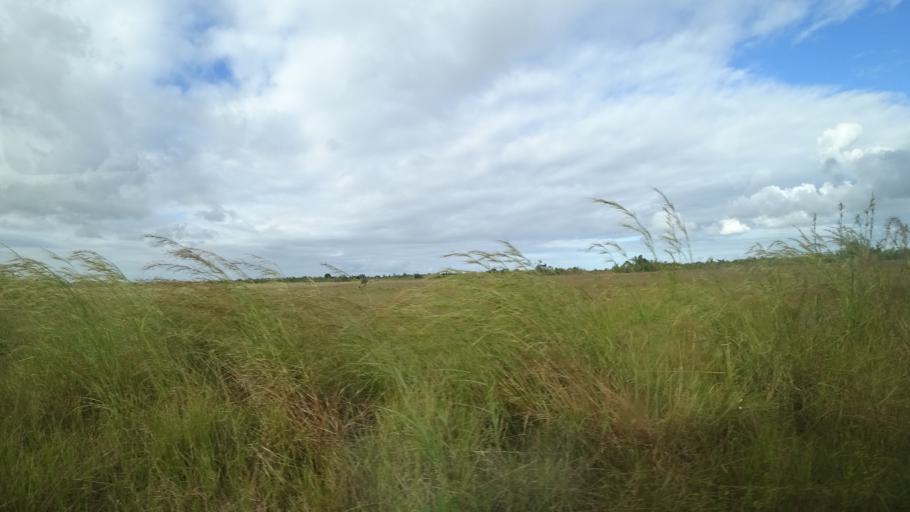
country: MZ
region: Sofala
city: Beira
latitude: -19.6388
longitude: 35.0593
